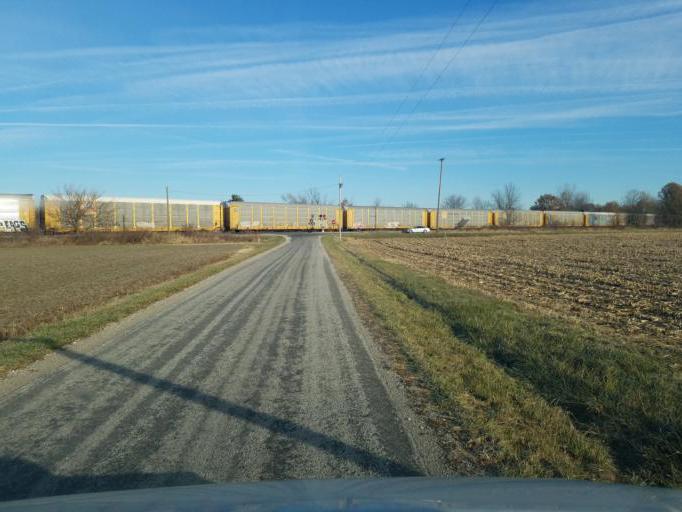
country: US
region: Ohio
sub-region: Morrow County
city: Mount Gilead
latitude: 40.6519
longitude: -82.9387
